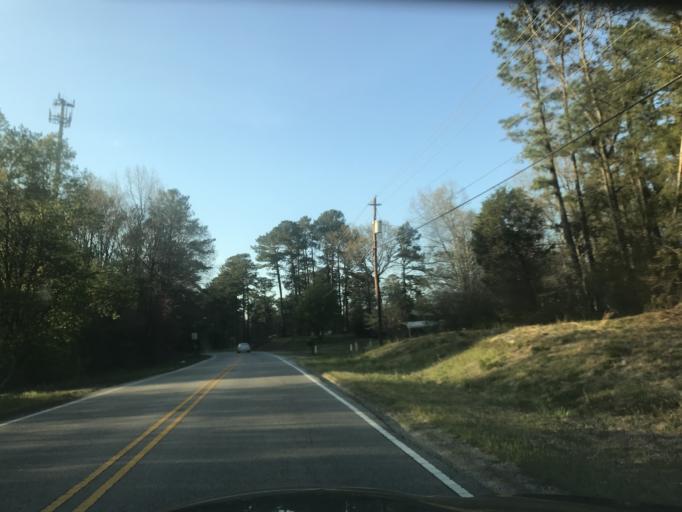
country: US
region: North Carolina
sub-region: Wake County
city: Knightdale
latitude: 35.7513
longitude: -78.5349
